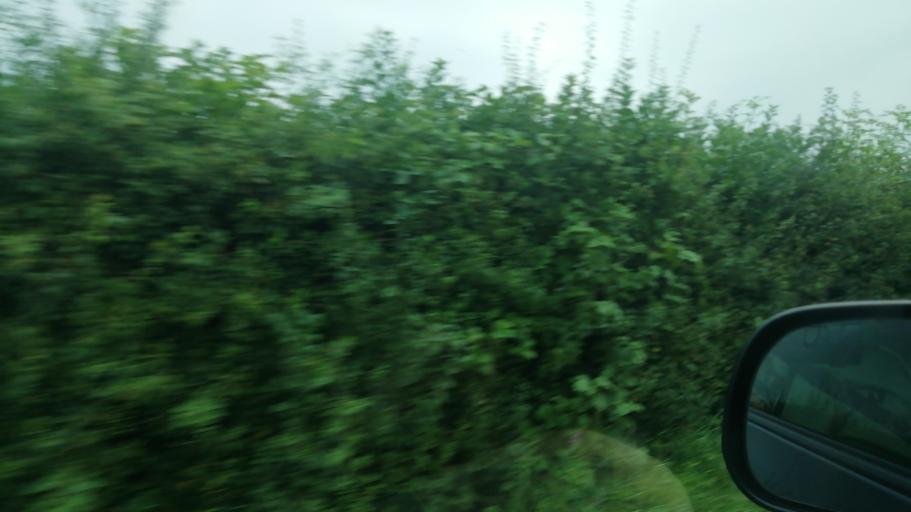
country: IE
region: Munster
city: Fethard
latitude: 52.5190
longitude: -7.6835
